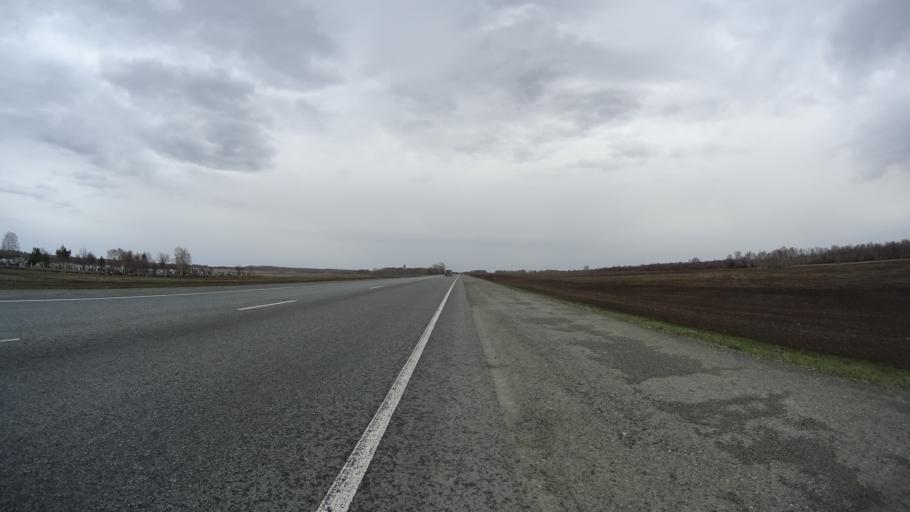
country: RU
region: Chelyabinsk
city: Krasnogorskiy
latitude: 54.6693
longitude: 61.2512
